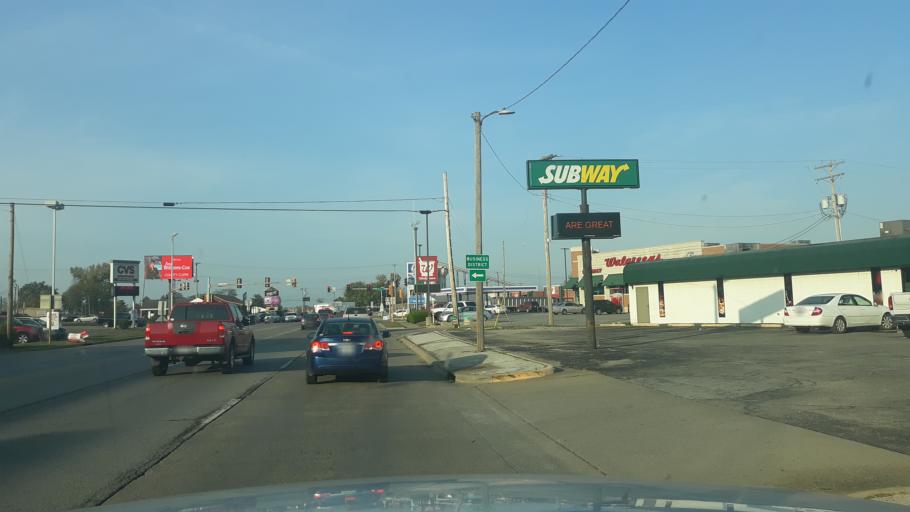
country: US
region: Illinois
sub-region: Saline County
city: Harrisburg
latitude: 37.7373
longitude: -88.5330
